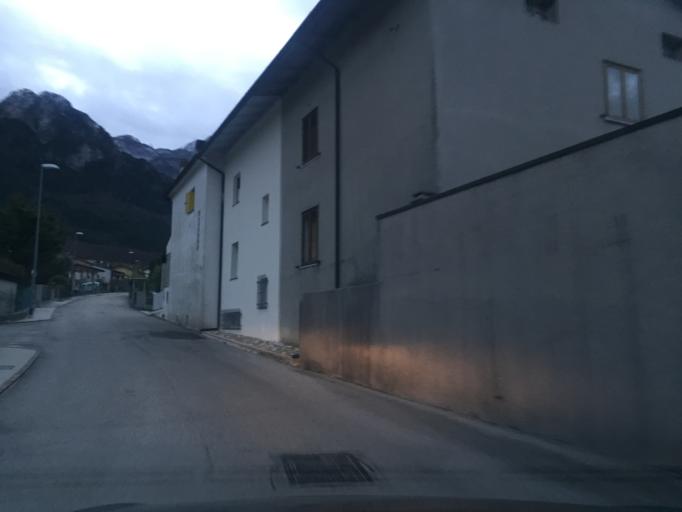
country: IT
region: Friuli Venezia Giulia
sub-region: Provincia di Udine
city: Venzone
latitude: 46.3248
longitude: 13.1361
